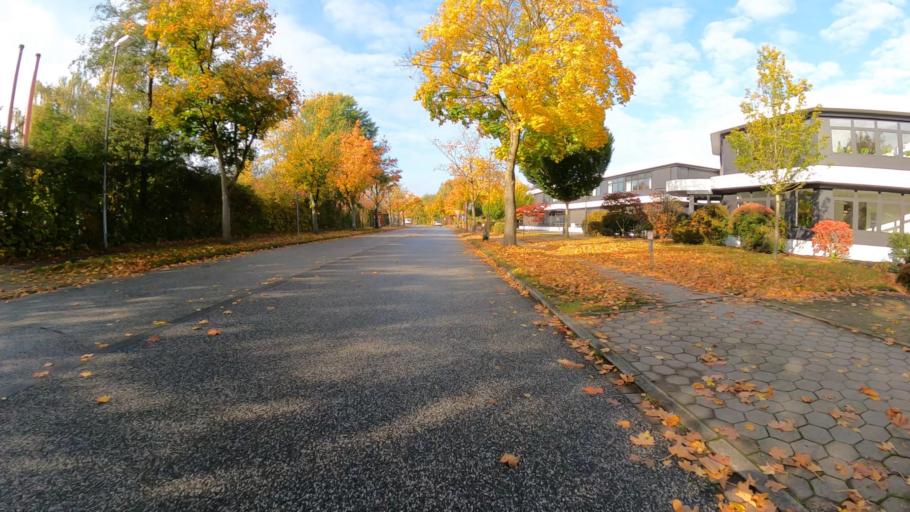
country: DE
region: Schleswig-Holstein
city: Delingsdorf
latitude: 53.6895
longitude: 10.2625
